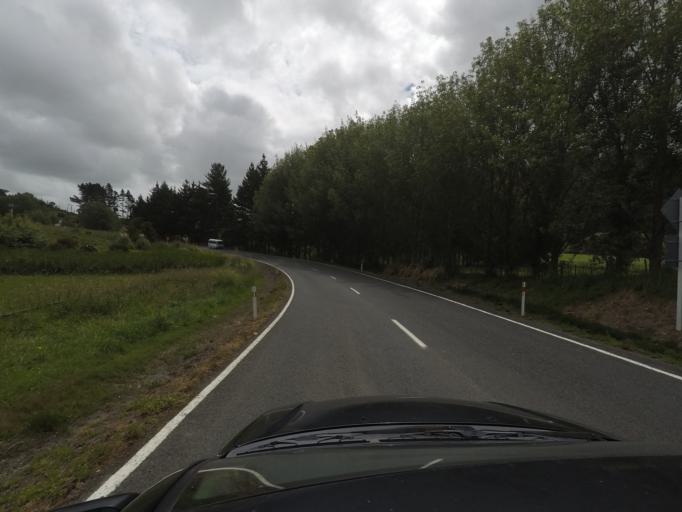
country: NZ
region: Auckland
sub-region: Auckland
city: Parakai
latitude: -36.5008
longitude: 174.4848
